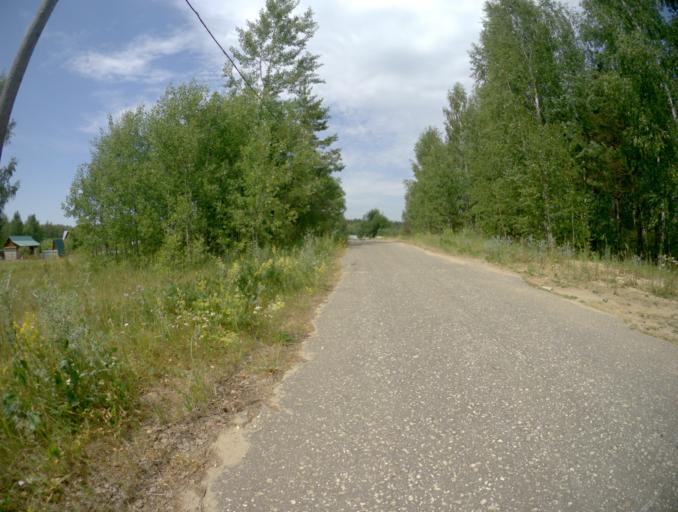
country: RU
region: Vladimir
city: Raduzhnyy
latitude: 56.0228
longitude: 40.2359
